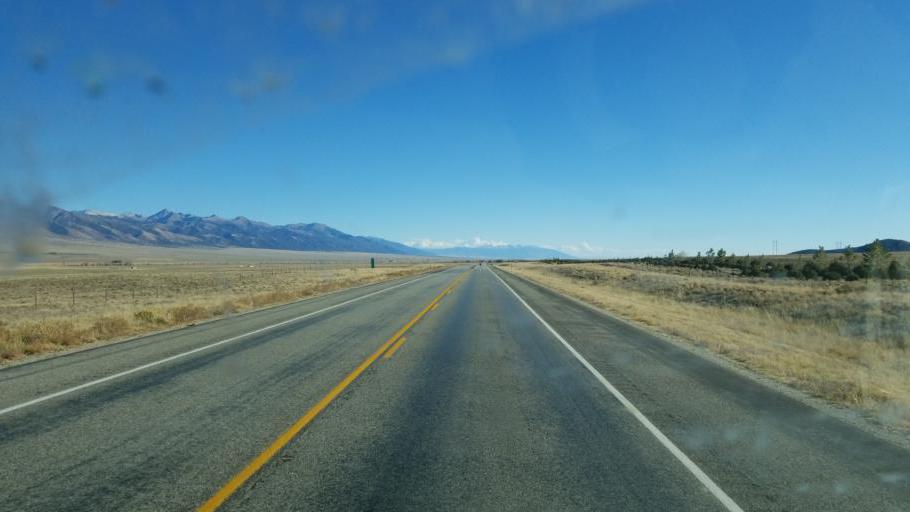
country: US
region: Colorado
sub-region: Saguache County
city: Saguache
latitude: 38.2778
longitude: -105.9718
